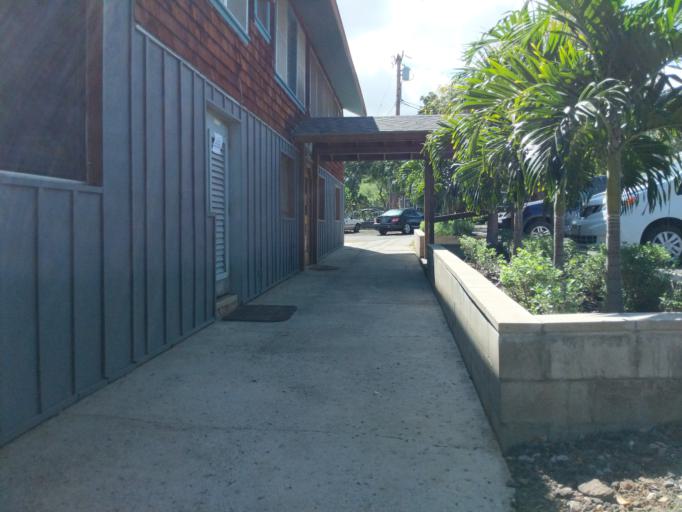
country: US
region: Hawaii
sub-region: Honolulu County
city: Waianae
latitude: 21.4402
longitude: -158.1559
